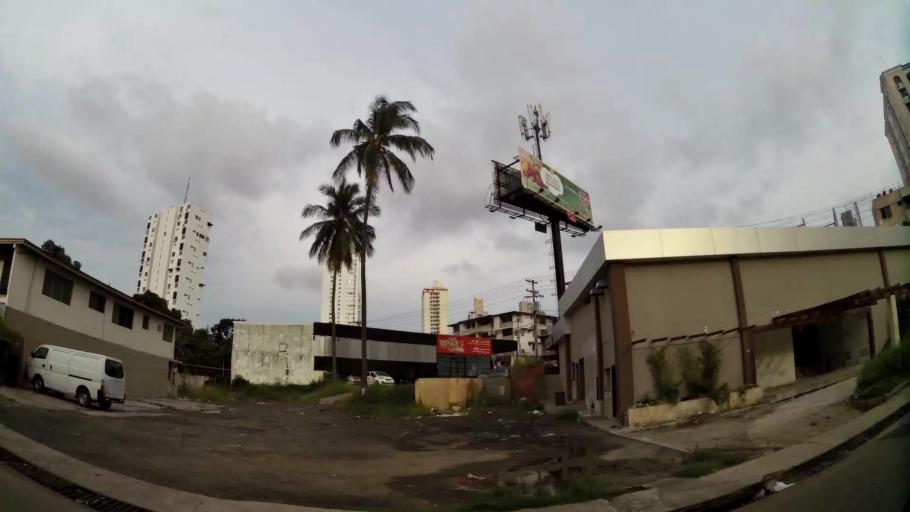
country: PA
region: Panama
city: Panama
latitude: 8.9940
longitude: -79.5166
